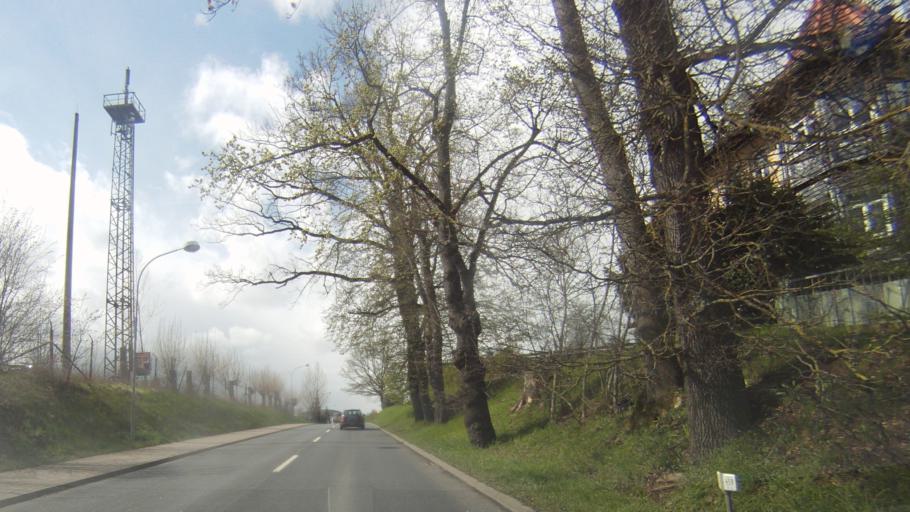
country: DE
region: Thuringia
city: Schalkau
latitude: 50.4000
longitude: 10.9996
